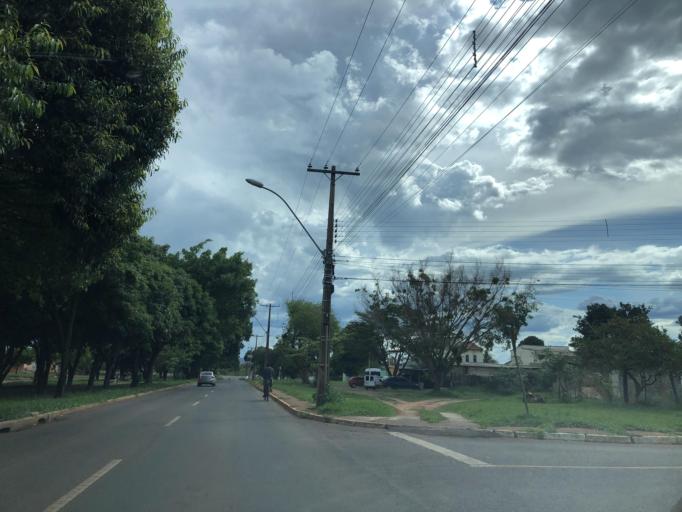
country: BR
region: Goias
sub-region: Luziania
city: Luziania
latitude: -16.0304
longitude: -48.0744
